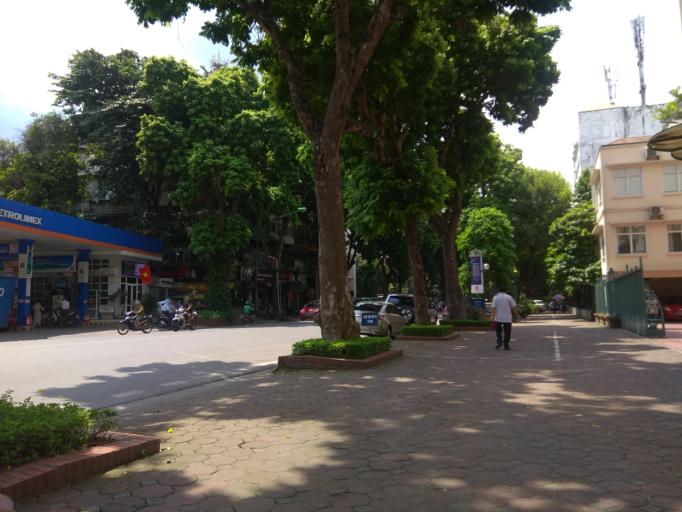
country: VN
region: Ha Noi
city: Hoan Kiem
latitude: 21.0193
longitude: 105.8585
